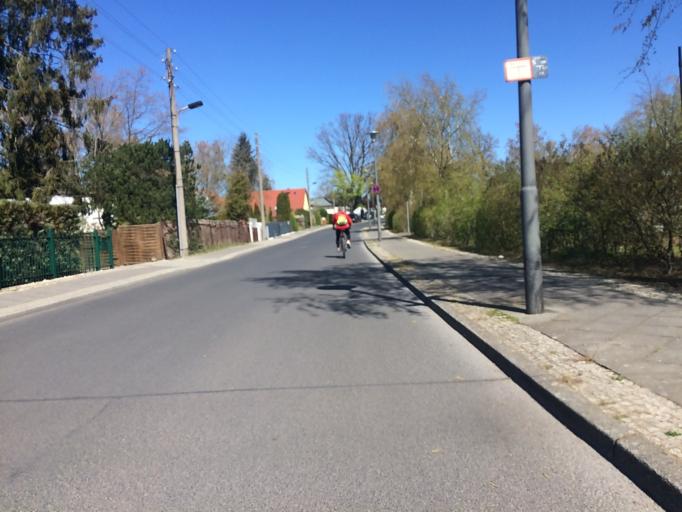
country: DE
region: Berlin
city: Rahnsdorf
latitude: 52.4307
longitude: 13.7131
